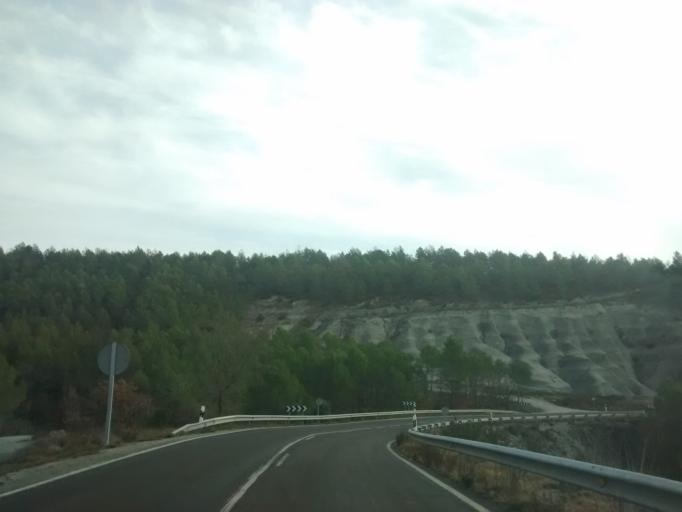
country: ES
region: Aragon
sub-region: Provincia de Zaragoza
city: Undues de Lerda
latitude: 42.6165
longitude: -1.1120
